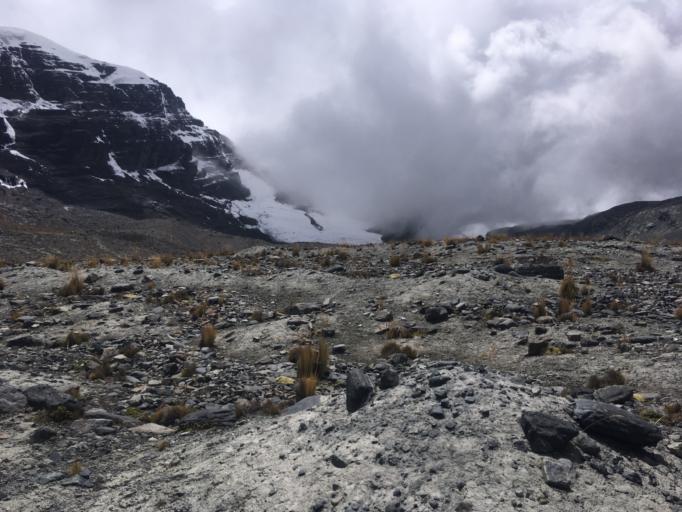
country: BO
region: La Paz
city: La Paz
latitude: -16.3969
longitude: -67.9532
